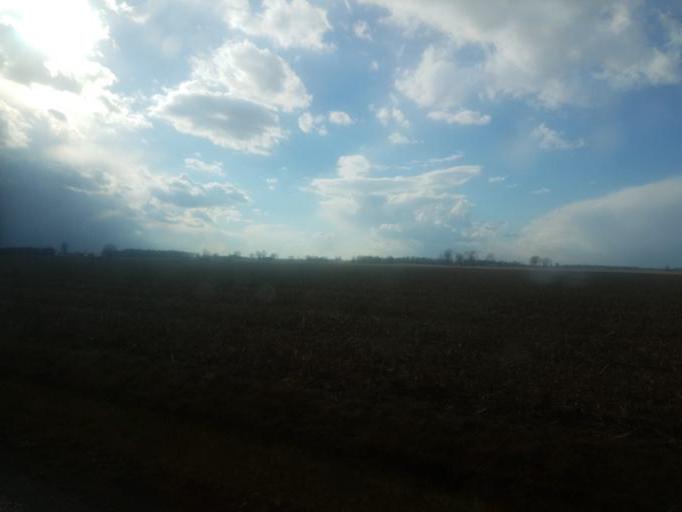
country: US
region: Ohio
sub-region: Marion County
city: Prospect
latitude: 40.4799
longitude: -83.1178
